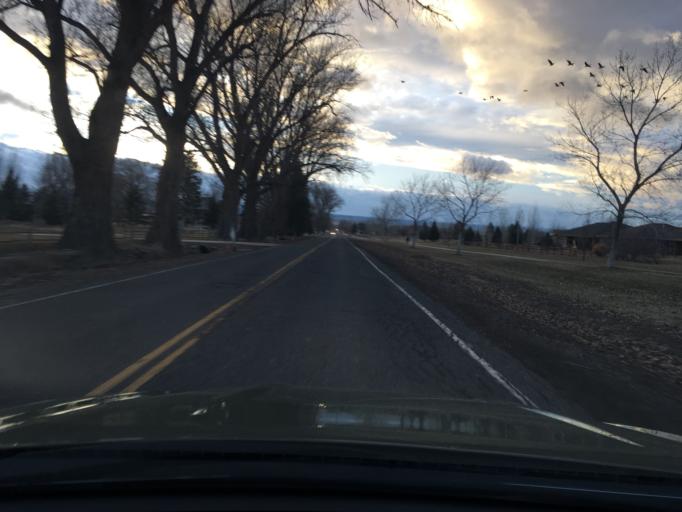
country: US
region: Colorado
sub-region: Montrose County
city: Montrose
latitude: 38.4817
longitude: -107.8353
